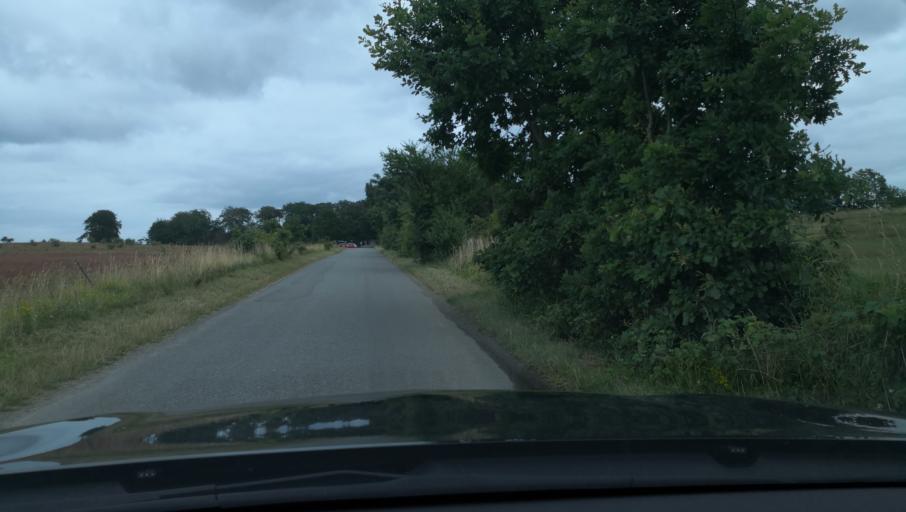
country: SE
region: Skane
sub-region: Simrishamns Kommun
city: Kivik
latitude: 55.7241
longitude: 14.1876
